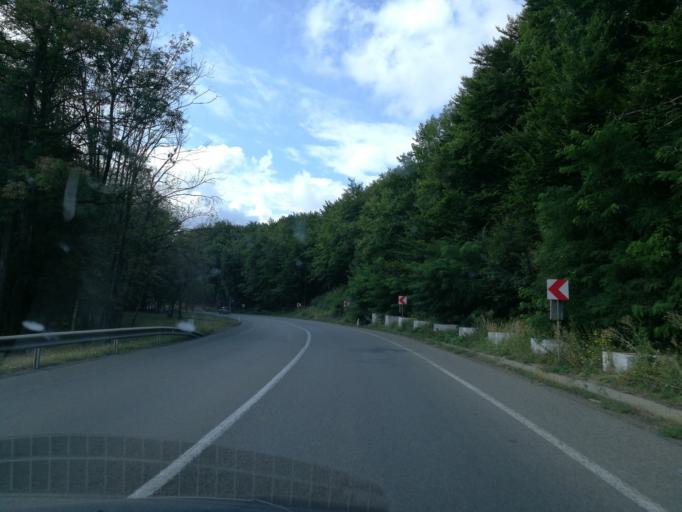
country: RO
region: Suceava
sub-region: Comuna Ilisesti
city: Ilisesti
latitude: 47.6060
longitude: 26.0206
